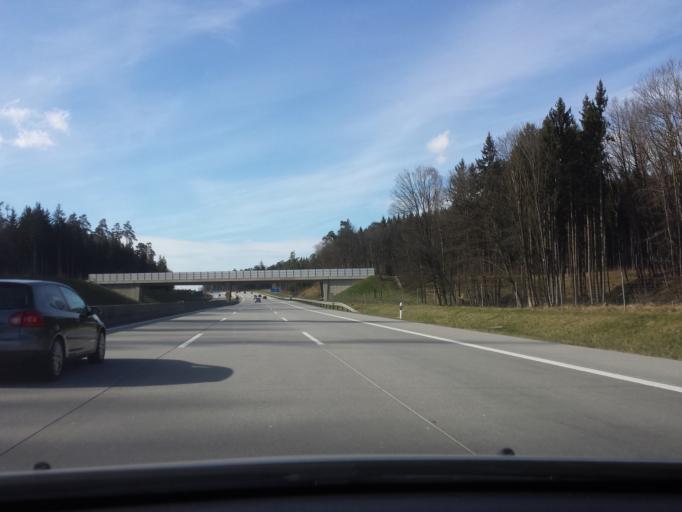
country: DE
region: Bavaria
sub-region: Swabia
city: Adelzhausen
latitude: 48.3340
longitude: 11.1624
